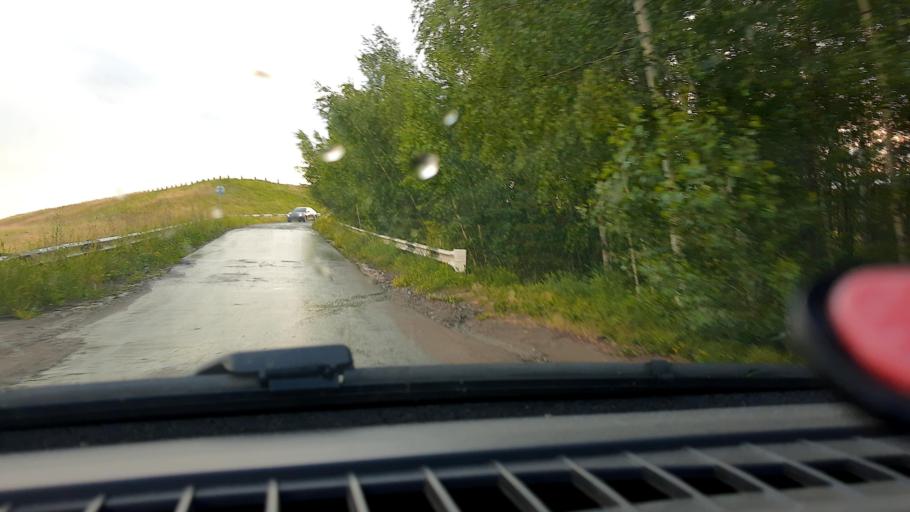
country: RU
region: Nizjnij Novgorod
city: Zavolzh'ye
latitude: 56.6758
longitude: 43.4134
